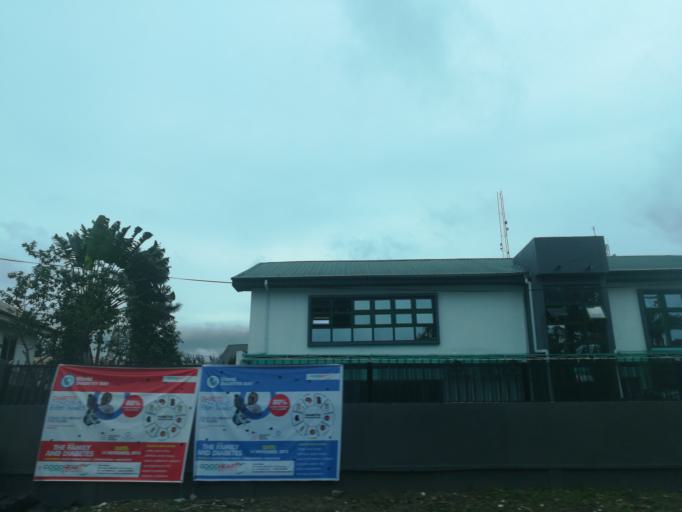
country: NG
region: Rivers
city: Port Harcourt
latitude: 4.8199
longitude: 7.0006
